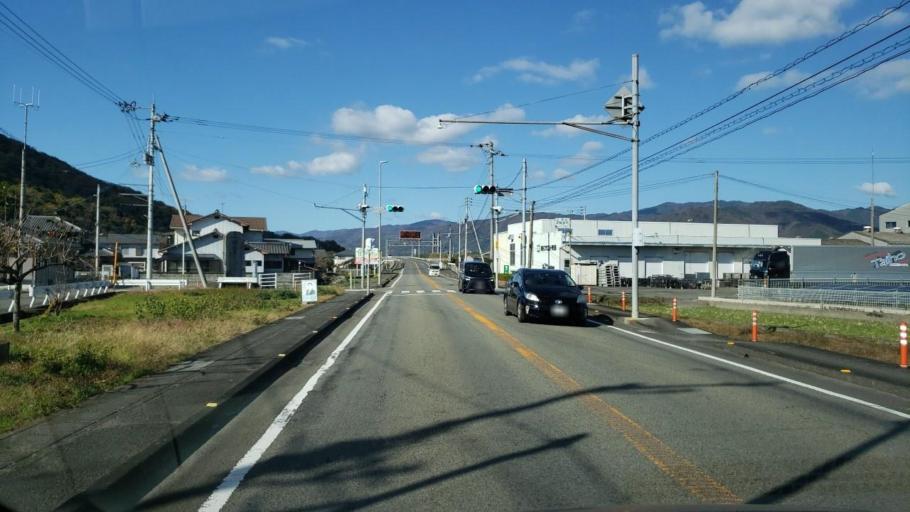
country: JP
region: Tokushima
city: Wakimachi
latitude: 34.0615
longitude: 134.2069
